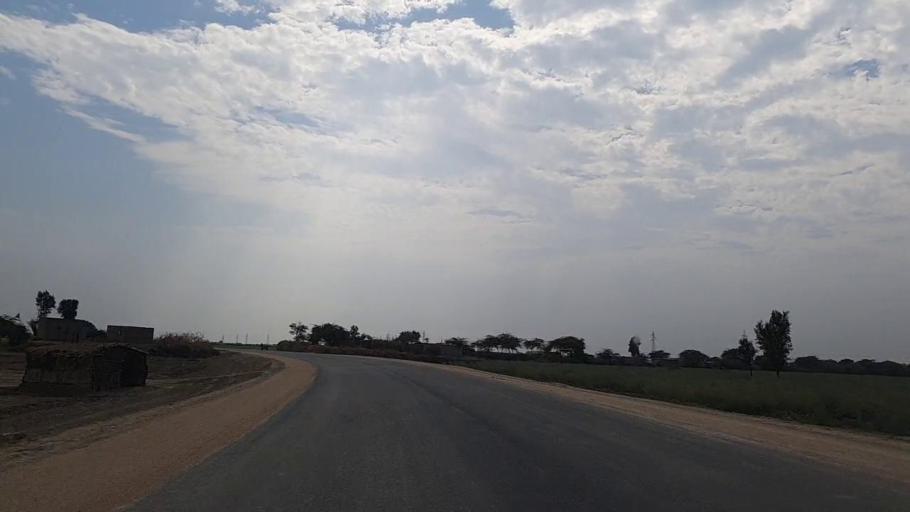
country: PK
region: Sindh
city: Naukot
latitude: 24.9692
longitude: 69.2829
